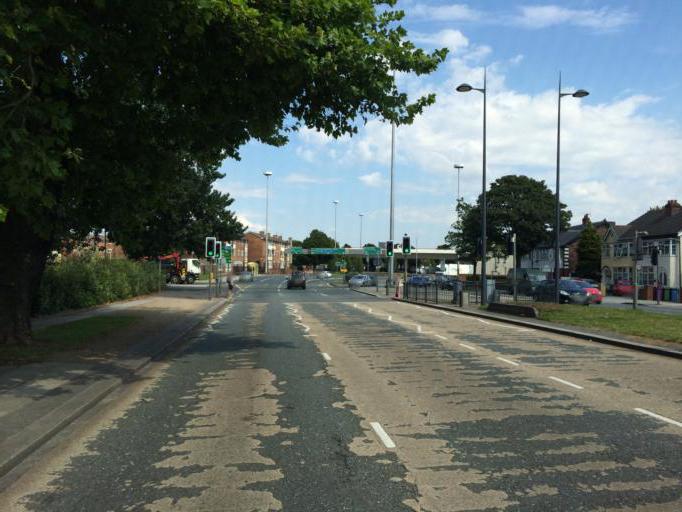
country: GB
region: England
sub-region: Knowsley
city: Huyton
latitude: 53.4077
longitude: -2.9051
